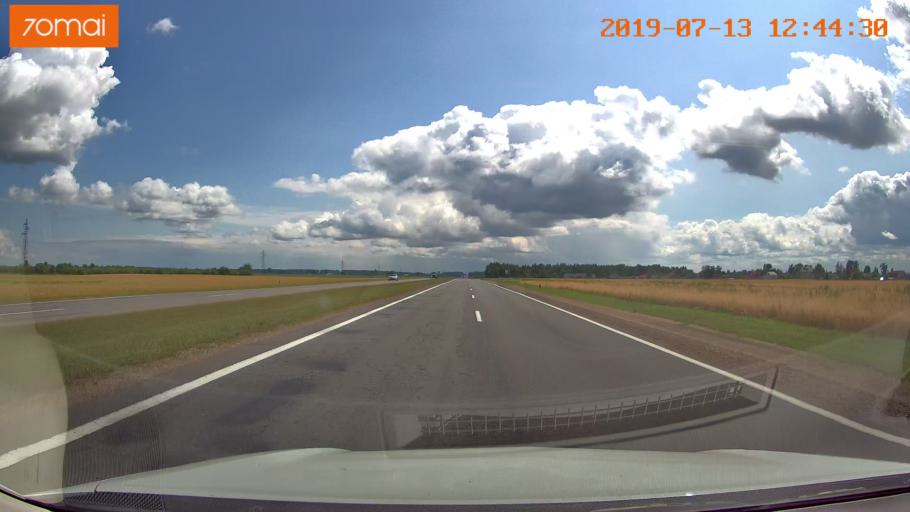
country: BY
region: Minsk
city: Dukora
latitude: 53.6390
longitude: 28.0013
